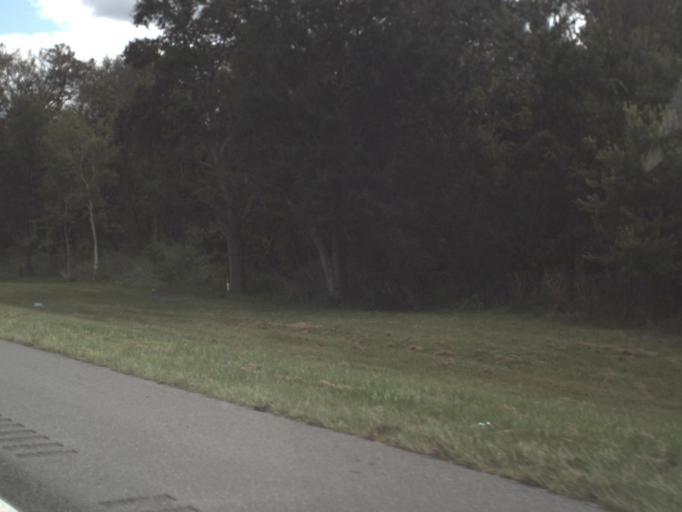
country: US
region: Florida
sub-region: Orange County
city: Winter Garden
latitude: 28.5450
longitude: -81.5967
